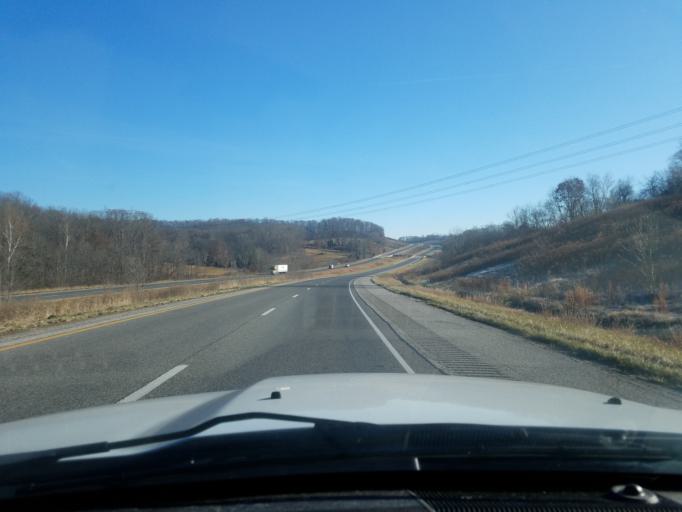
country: US
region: Indiana
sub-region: Dubois County
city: Ferdinand
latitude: 38.2154
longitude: -86.7407
